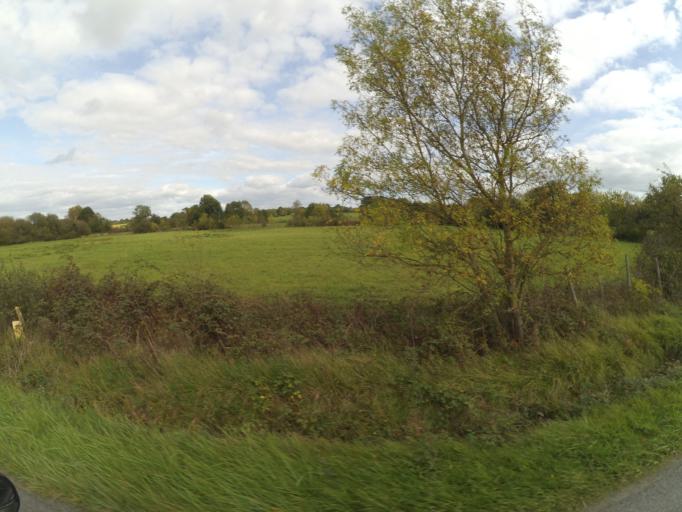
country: FR
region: Pays de la Loire
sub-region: Departement de la Loire-Atlantique
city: Bouvron
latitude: 47.4650
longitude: -1.8355
